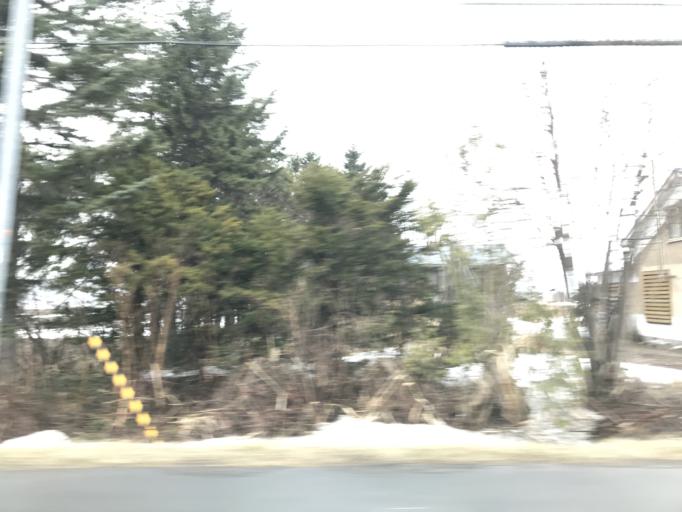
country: JP
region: Hokkaido
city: Nayoro
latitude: 44.2347
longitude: 142.3947
